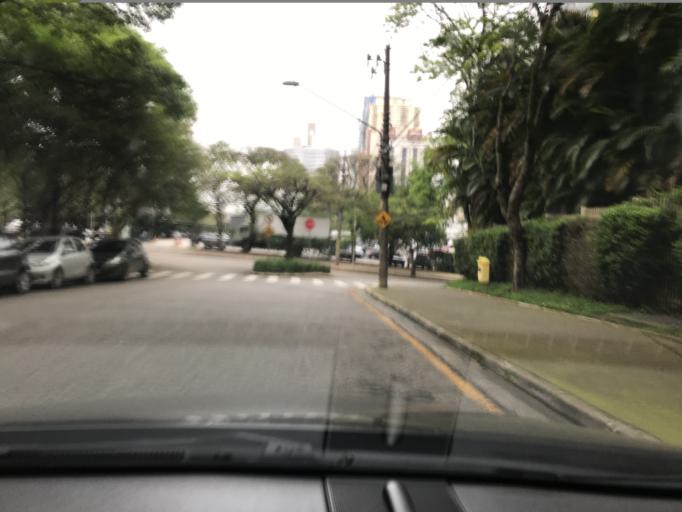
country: BR
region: Sao Paulo
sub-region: Carapicuiba
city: Carapicuiba
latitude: -23.4946
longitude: -46.8466
